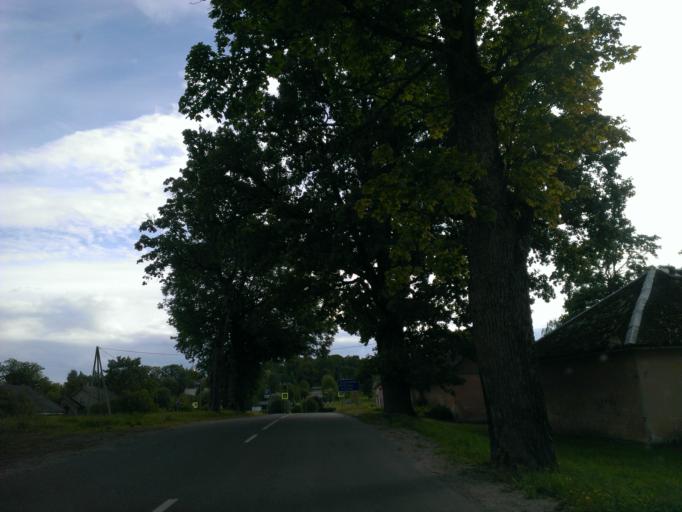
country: LV
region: Malpils
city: Malpils
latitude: 56.8949
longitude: 25.1817
